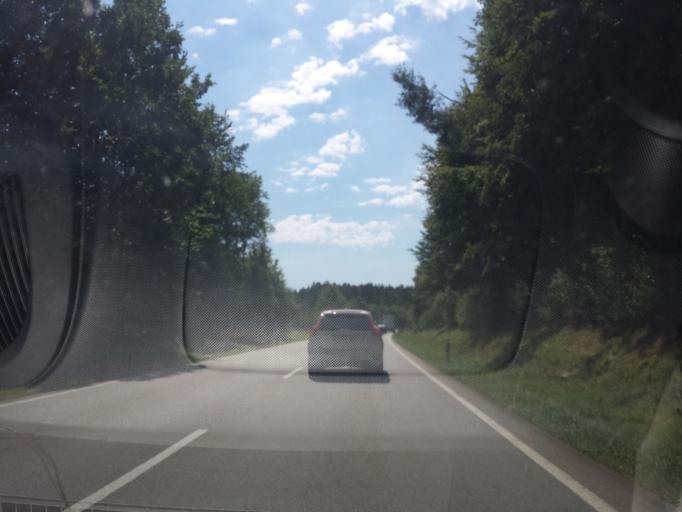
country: DE
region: Bavaria
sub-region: Lower Bavaria
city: Ascha
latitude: 49.0148
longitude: 12.6436
